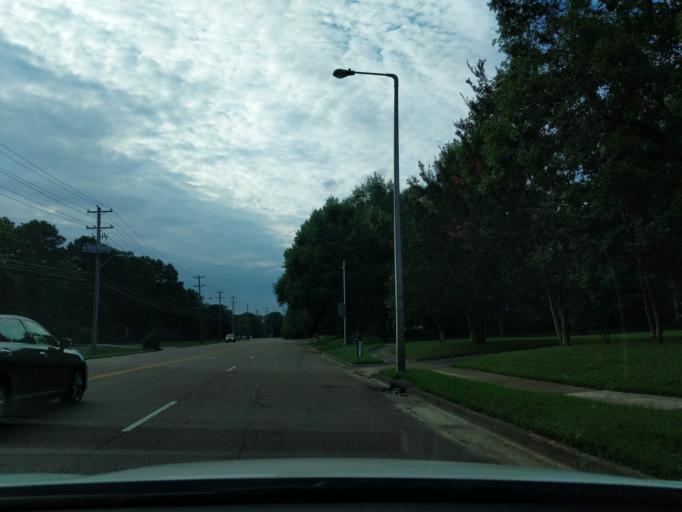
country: US
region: Tennessee
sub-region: Shelby County
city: Germantown
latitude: 35.0782
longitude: -89.7991
